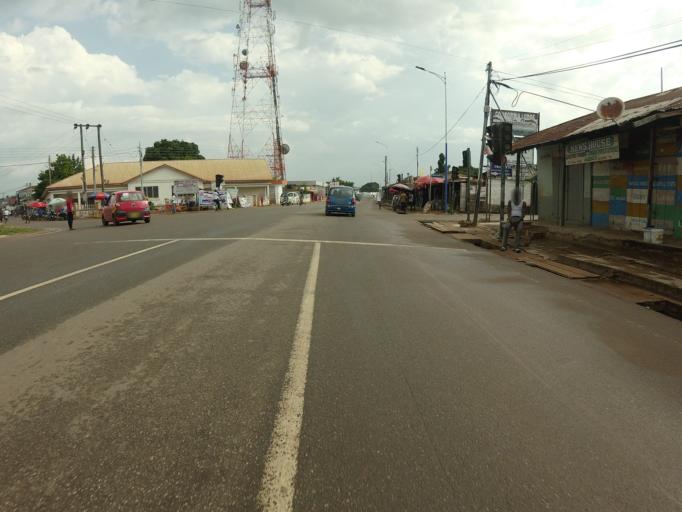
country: GH
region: Volta
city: Hohoe
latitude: 7.1532
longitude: 0.4760
